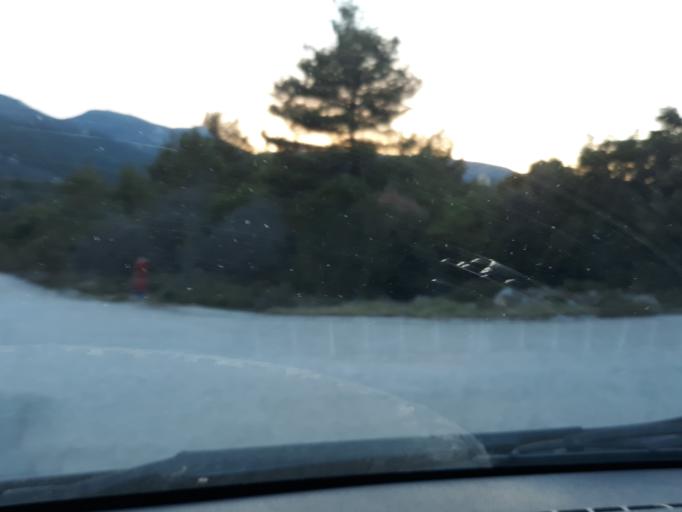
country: GR
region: Attica
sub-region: Nomarchia Anatolikis Attikis
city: Afidnes
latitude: 38.1933
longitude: 23.7966
